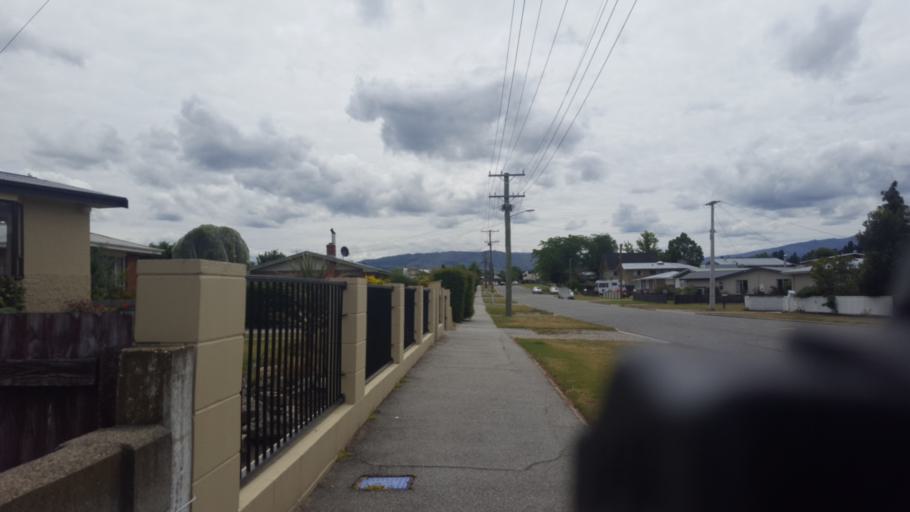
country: NZ
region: Otago
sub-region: Queenstown-Lakes District
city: Wanaka
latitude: -45.2486
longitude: 169.3804
